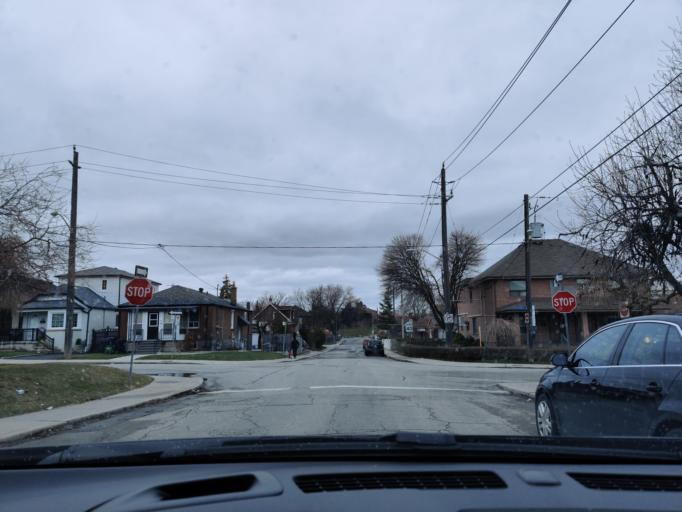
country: CA
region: Ontario
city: Toronto
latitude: 43.6976
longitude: -79.4478
